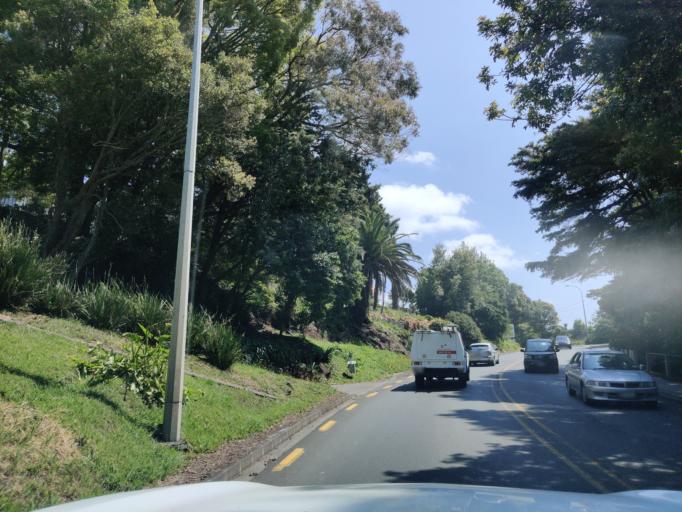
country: NZ
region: Auckland
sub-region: Auckland
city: Pukekohe East
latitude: -37.1983
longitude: 174.9123
